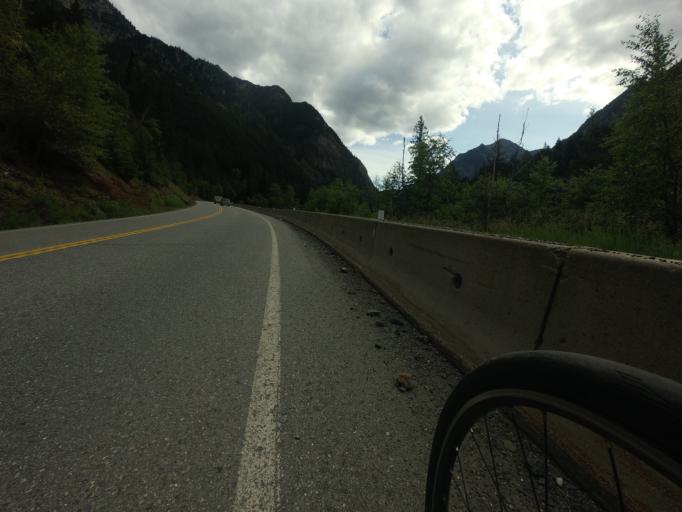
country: CA
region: British Columbia
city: Lillooet
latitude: 50.6364
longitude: -122.0890
